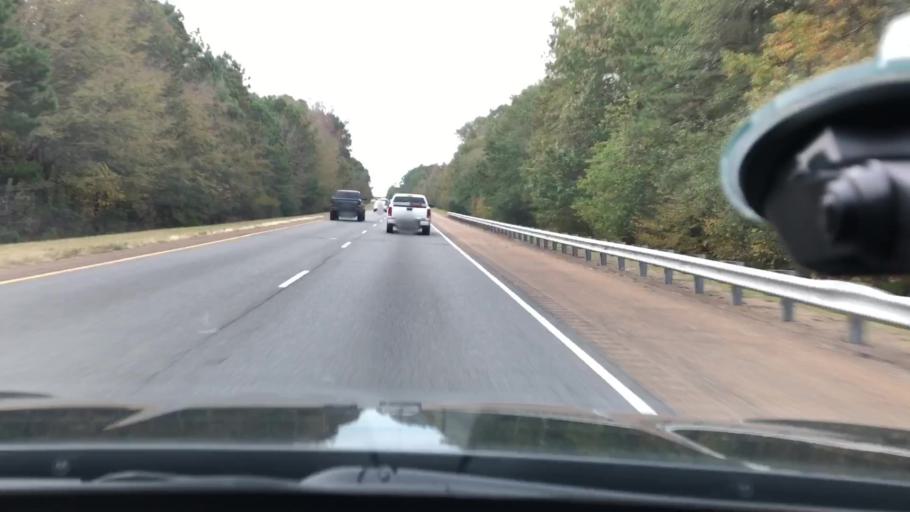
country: US
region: Arkansas
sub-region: Nevada County
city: Prescott
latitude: 33.8731
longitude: -93.3376
